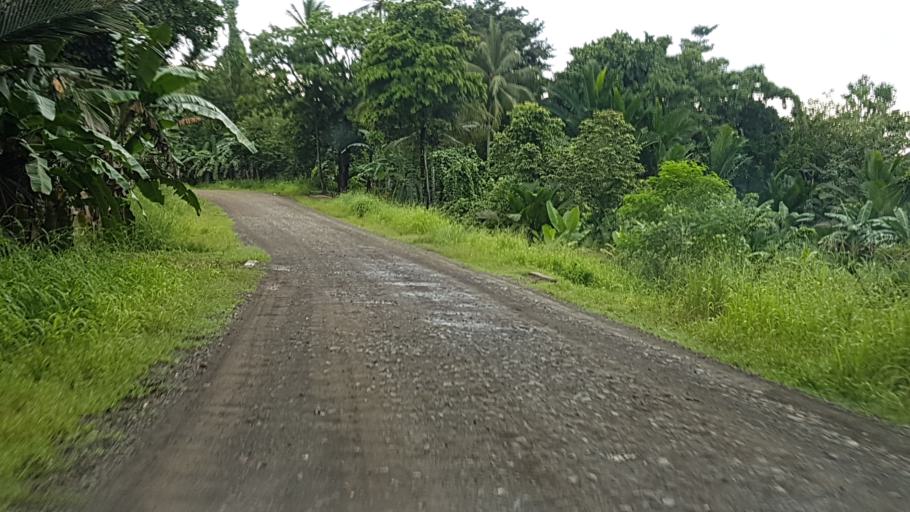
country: PG
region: Milne Bay
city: Alotau
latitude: -10.3428
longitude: 150.6336
